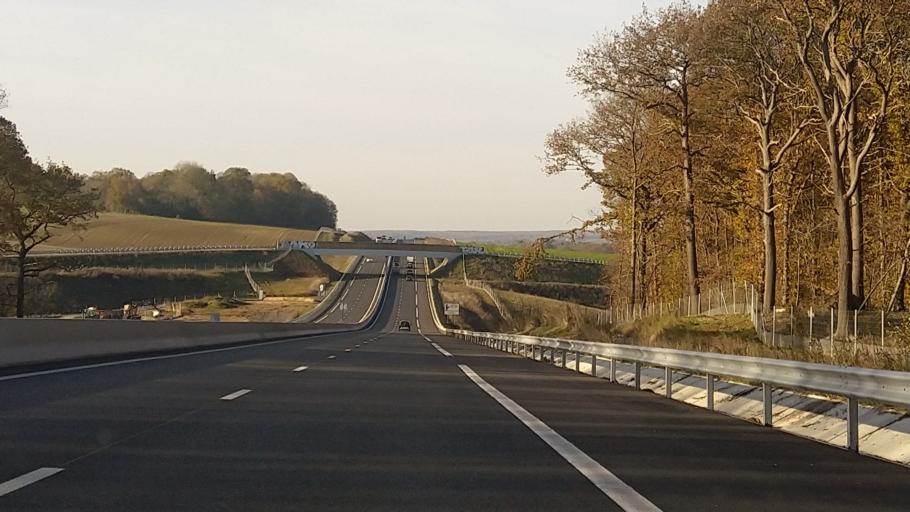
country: FR
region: Ile-de-France
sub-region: Departement du Val-d'Oise
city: Maffliers
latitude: 49.0914
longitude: 2.3059
